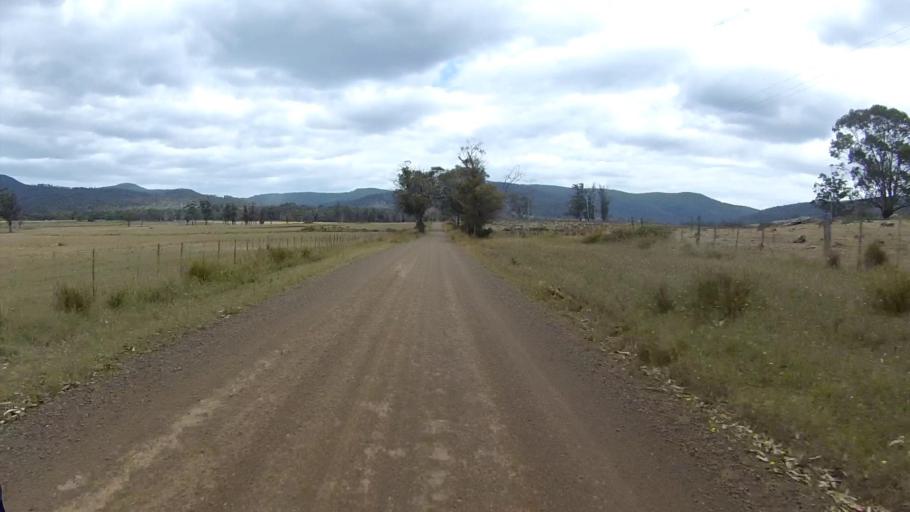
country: AU
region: Tasmania
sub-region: Sorell
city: Sorell
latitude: -42.6330
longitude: 147.9214
